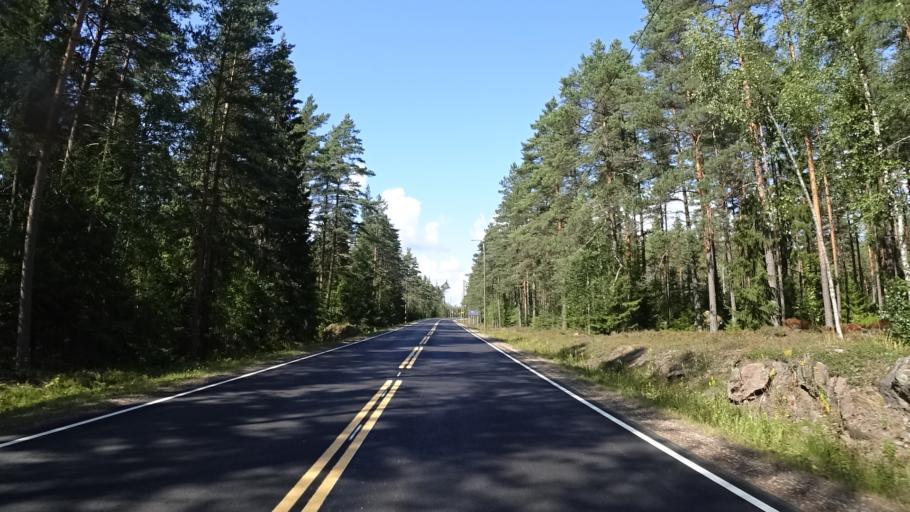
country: FI
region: Kymenlaakso
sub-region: Kotka-Hamina
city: Karhula
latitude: 60.5530
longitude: 26.9037
